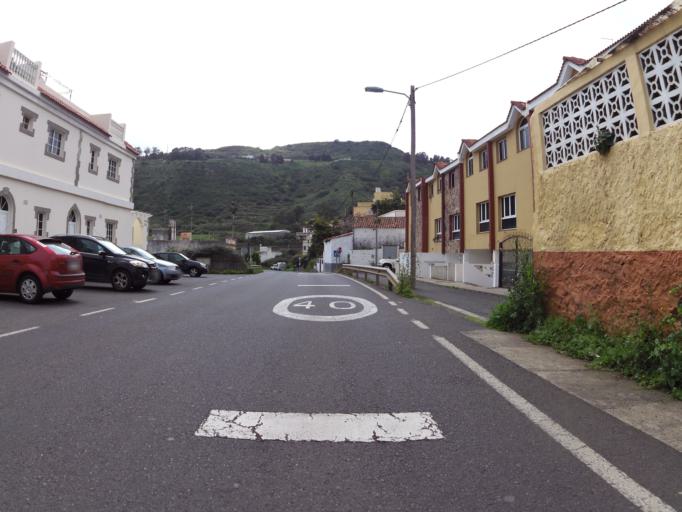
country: ES
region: Canary Islands
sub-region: Provincia de Las Palmas
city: Arucas
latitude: 28.0958
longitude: -15.5333
